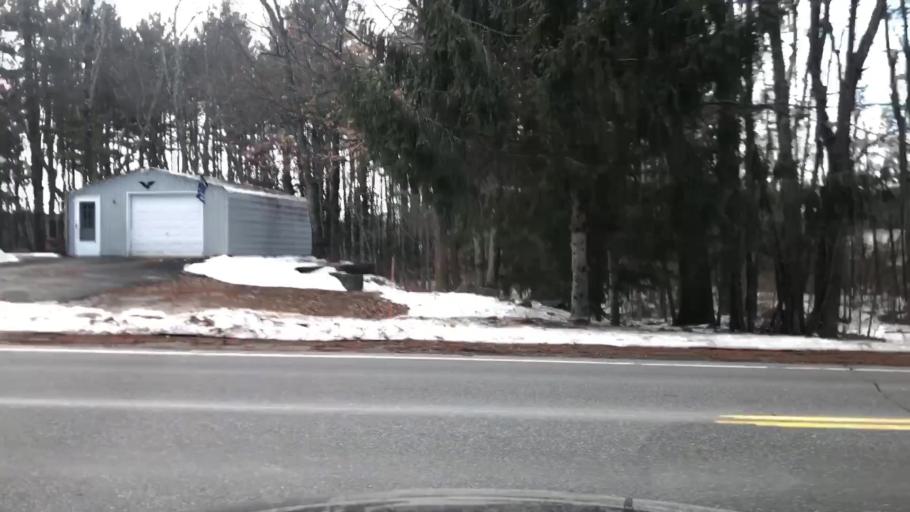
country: US
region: New Hampshire
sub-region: Hillsborough County
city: Milford
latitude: 42.8450
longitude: -71.6598
